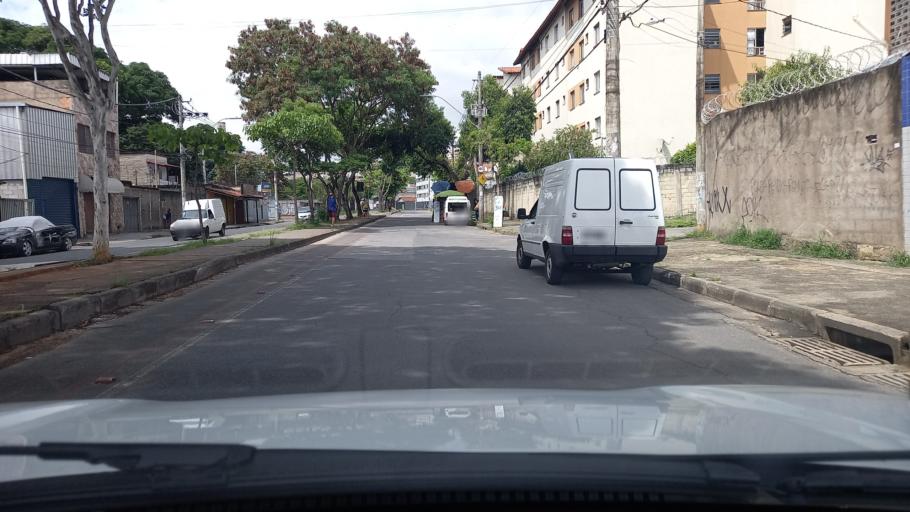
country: BR
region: Minas Gerais
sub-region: Contagem
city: Contagem
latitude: -19.8965
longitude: -44.0147
